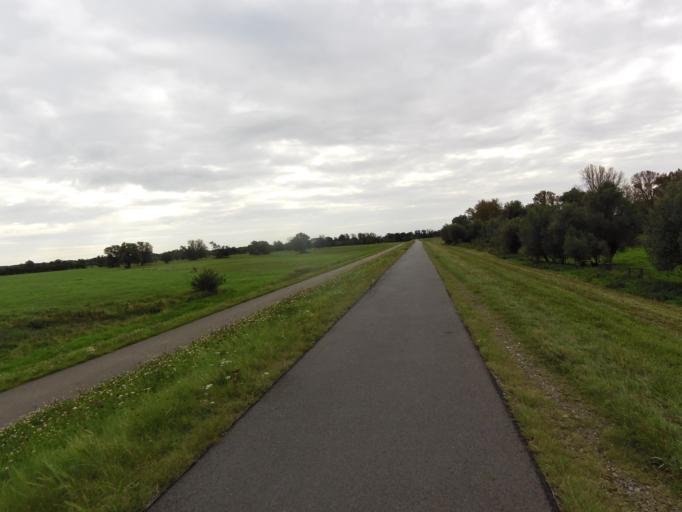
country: DE
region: Brandenburg
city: Breese
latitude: 52.9737
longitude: 11.7826
